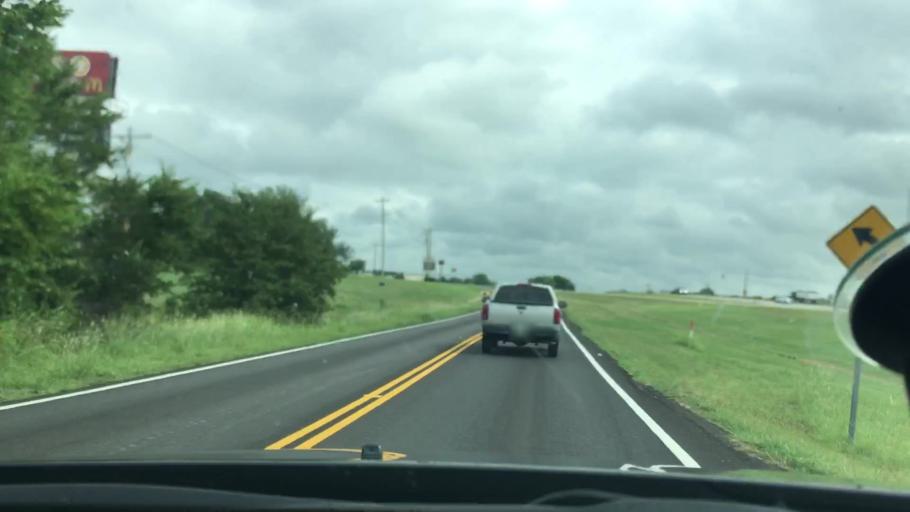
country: US
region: Oklahoma
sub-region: Bryan County
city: Durant
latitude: 34.0170
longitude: -96.3925
